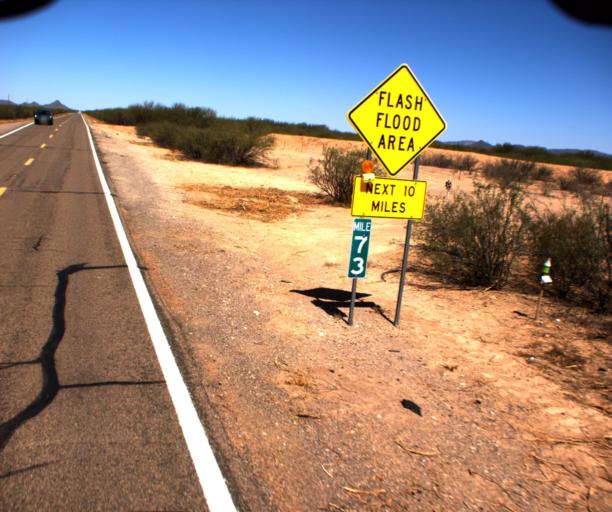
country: US
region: Arizona
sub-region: Pima County
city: Ajo
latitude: 32.1925
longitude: -112.4301
